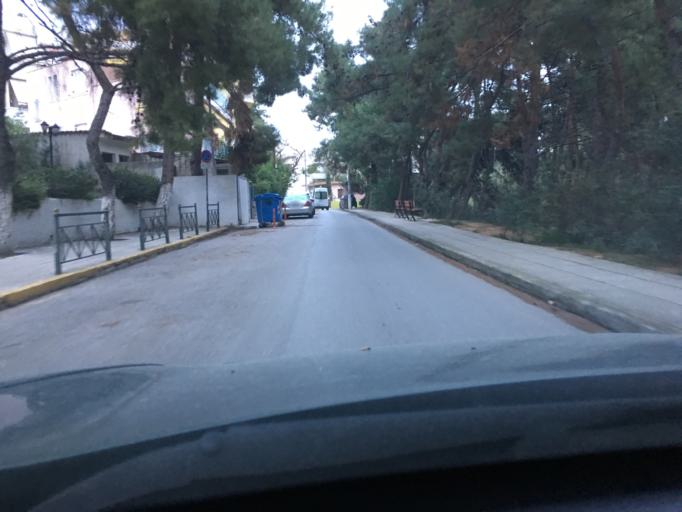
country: GR
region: Attica
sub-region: Nomarchia Athinas
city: Khalandrion
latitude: 38.0256
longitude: 23.8028
